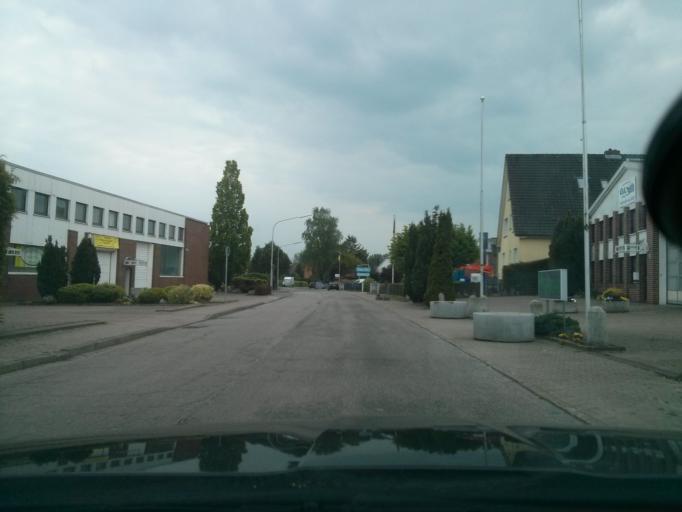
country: DE
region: Schleswig-Holstein
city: Halstenbek
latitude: 53.6320
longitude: 9.8554
